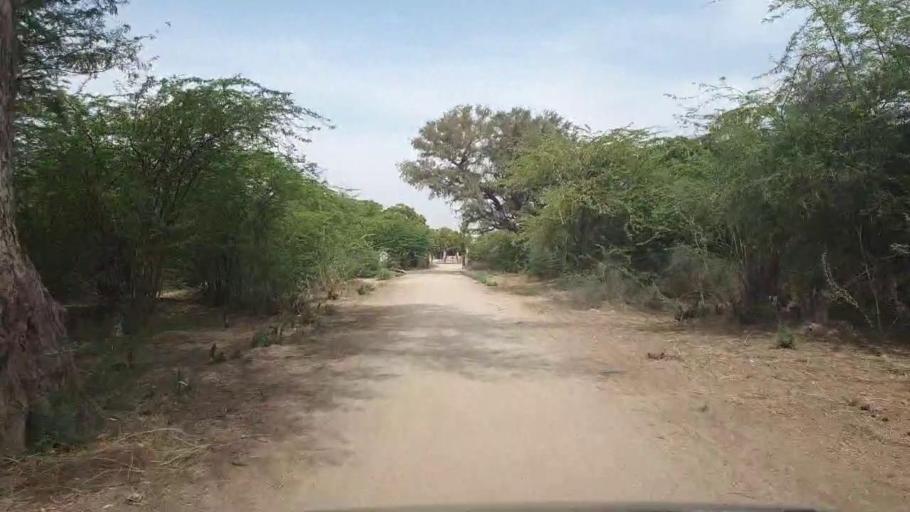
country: PK
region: Sindh
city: Umarkot
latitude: 25.2588
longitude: 69.7239
